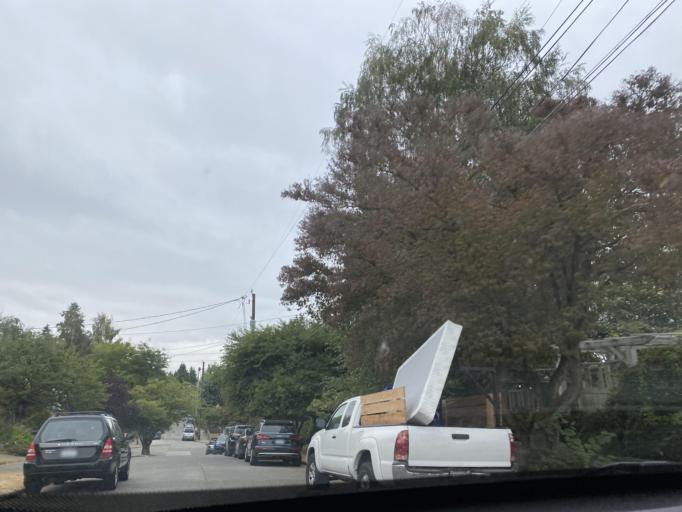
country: US
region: Washington
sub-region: King County
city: Seattle
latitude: 47.6474
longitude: -122.3736
